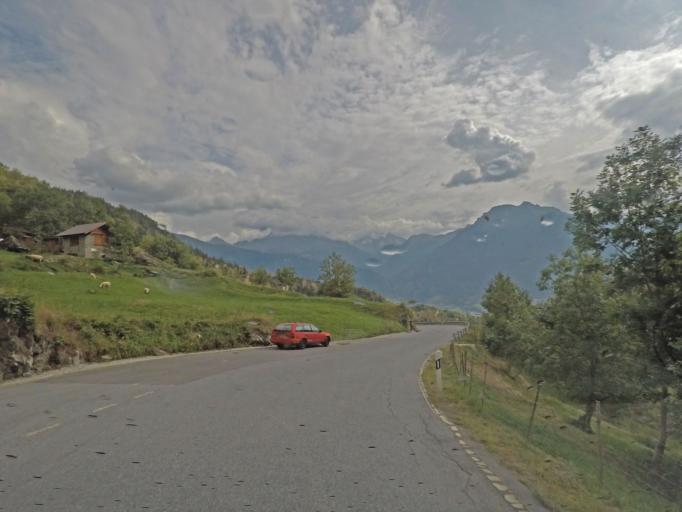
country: CH
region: Valais
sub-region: Brig District
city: Naters
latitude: 46.3506
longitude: 7.9816
